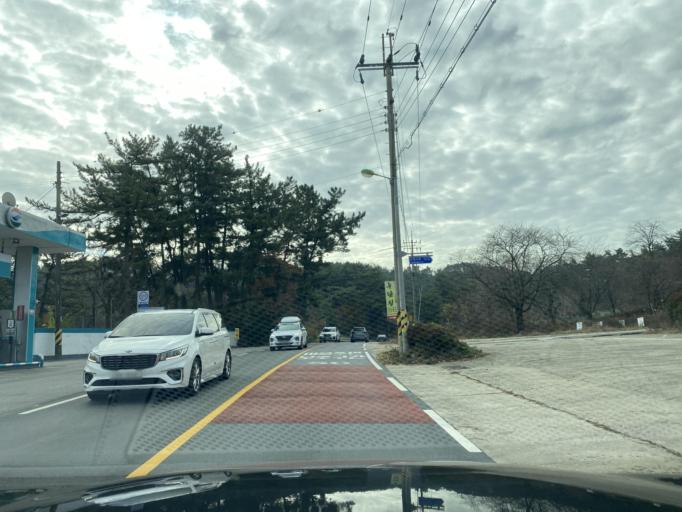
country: KR
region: Chungcheongnam-do
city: Hongsung
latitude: 36.6735
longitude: 126.6425
